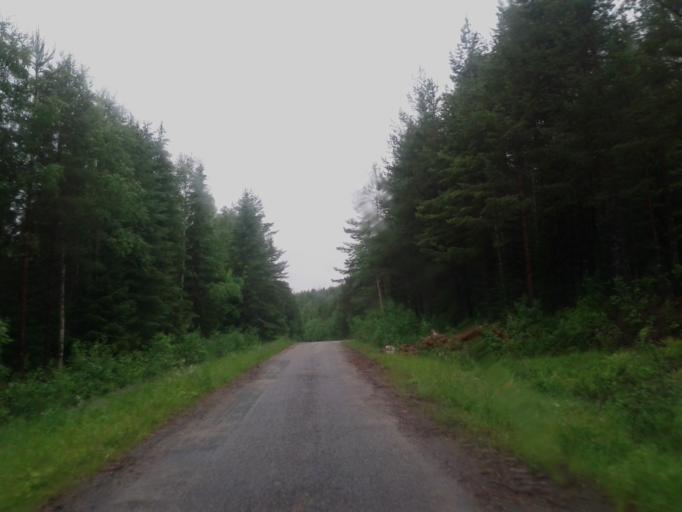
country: SE
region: Vaesternorrland
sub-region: Ange Kommun
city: Fransta
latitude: 62.3788
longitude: 16.3310
